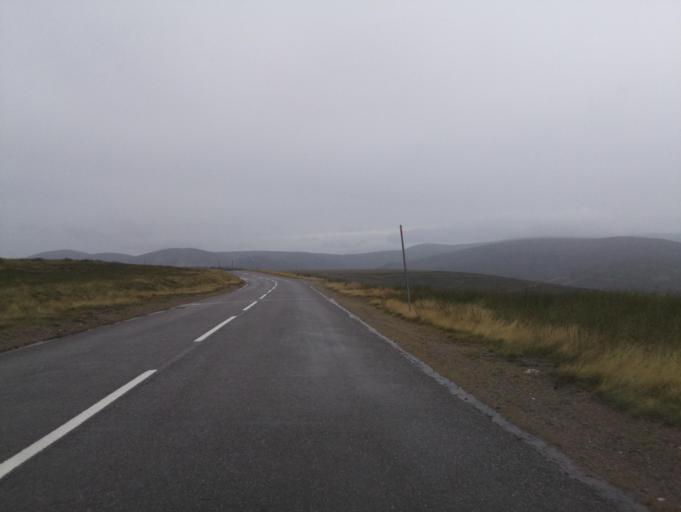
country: GB
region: Scotland
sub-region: Aberdeenshire
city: Ballater
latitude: 57.1850
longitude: -3.2383
